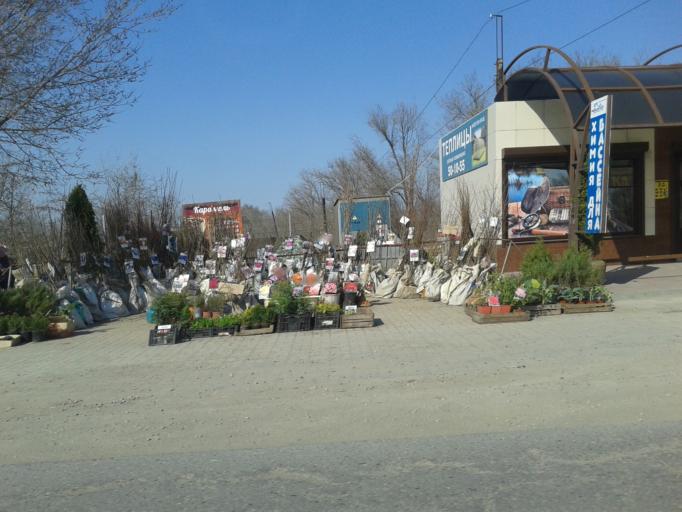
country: RU
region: Volgograd
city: Volgograd
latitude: 48.6295
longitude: 44.4256
